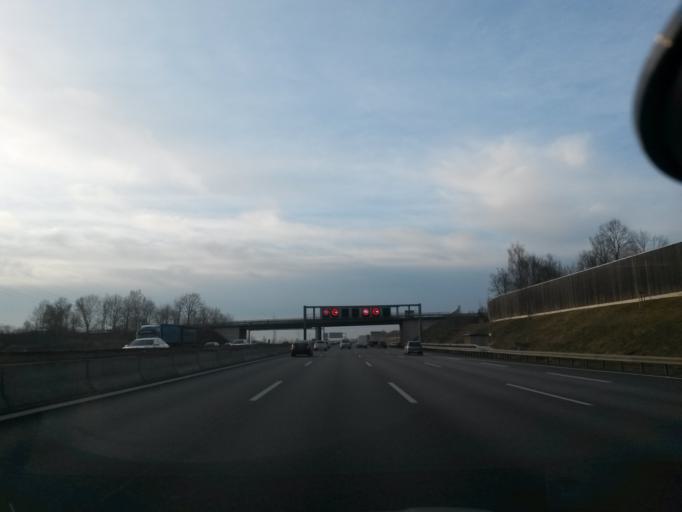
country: DE
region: Bavaria
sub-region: Upper Bavaria
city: Eching
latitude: 48.2964
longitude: 11.6328
